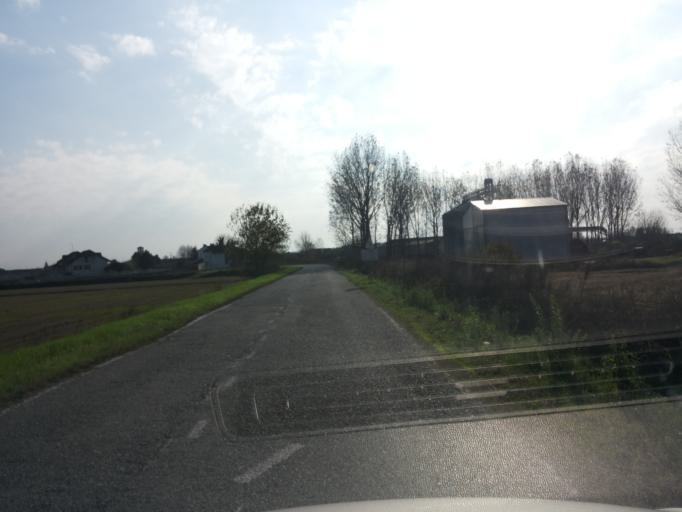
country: IT
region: Piedmont
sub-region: Provincia di Vercelli
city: Caresana
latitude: 45.2268
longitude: 8.4988
